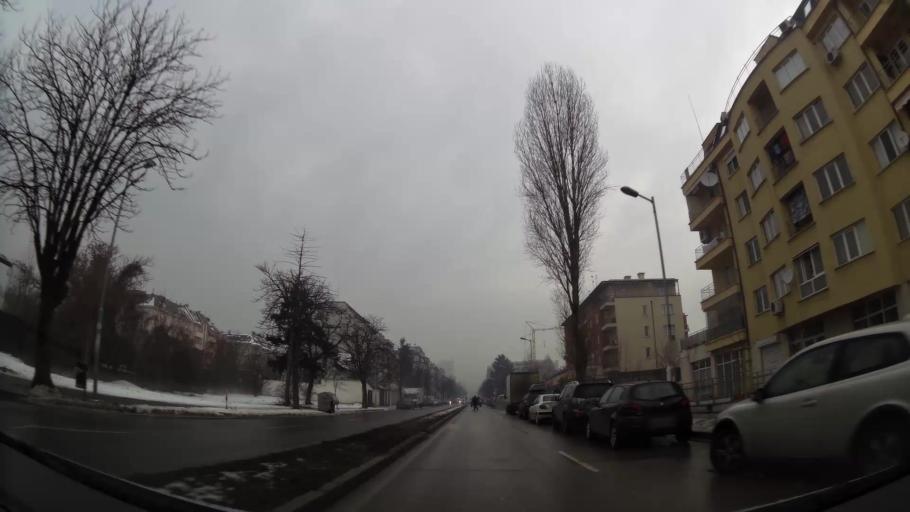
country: BG
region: Sofia-Capital
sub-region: Stolichna Obshtina
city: Sofia
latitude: 42.6746
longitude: 23.2603
